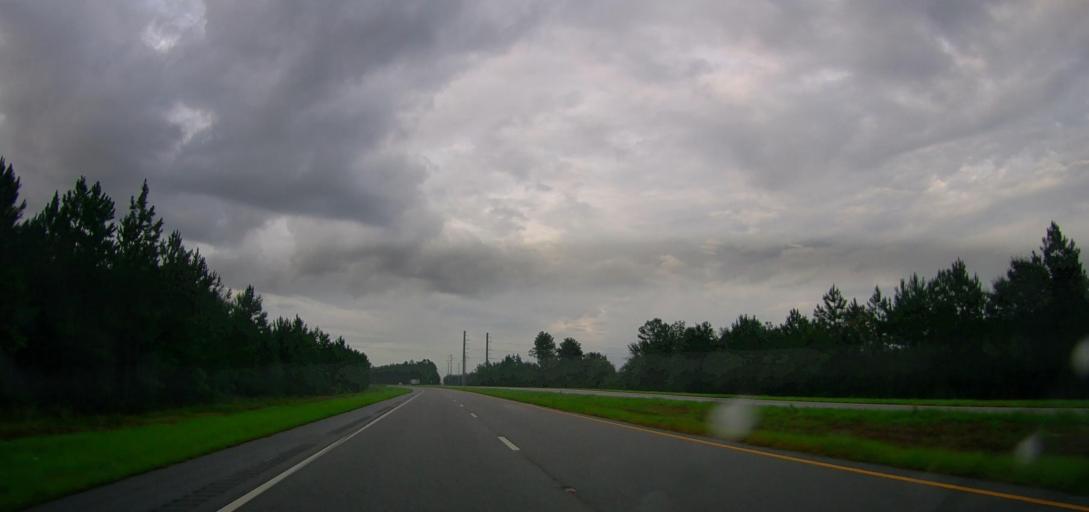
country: US
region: Georgia
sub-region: Ware County
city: Deenwood
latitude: 31.1653
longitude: -82.4153
